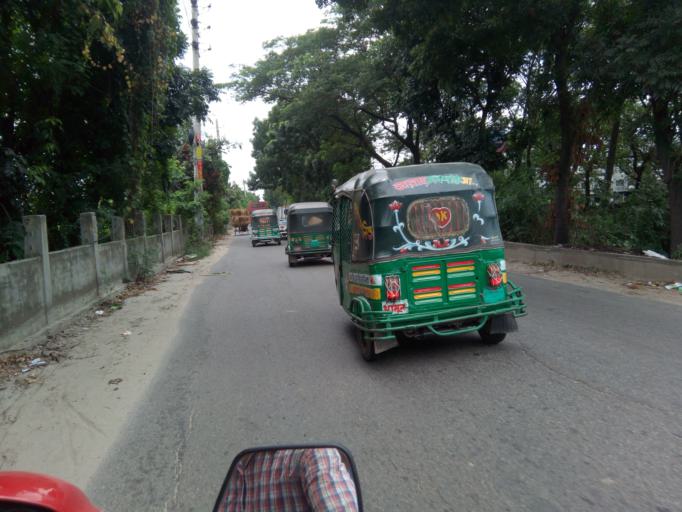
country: BD
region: Dhaka
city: Paltan
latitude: 23.7178
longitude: 90.4784
